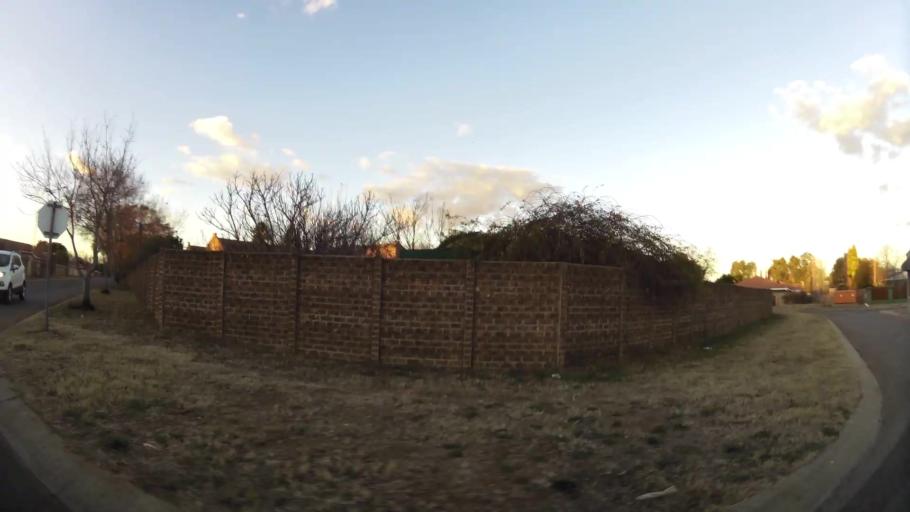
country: ZA
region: North-West
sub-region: Dr Kenneth Kaunda District Municipality
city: Potchefstroom
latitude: -26.7264
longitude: 27.1140
